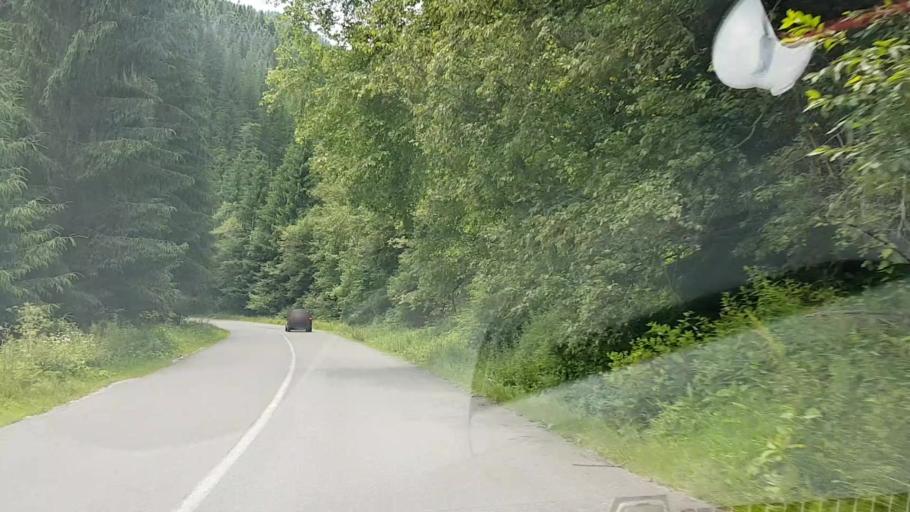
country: RO
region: Suceava
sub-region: Comuna Crucea
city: Crucea
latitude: 47.3513
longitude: 25.6051
